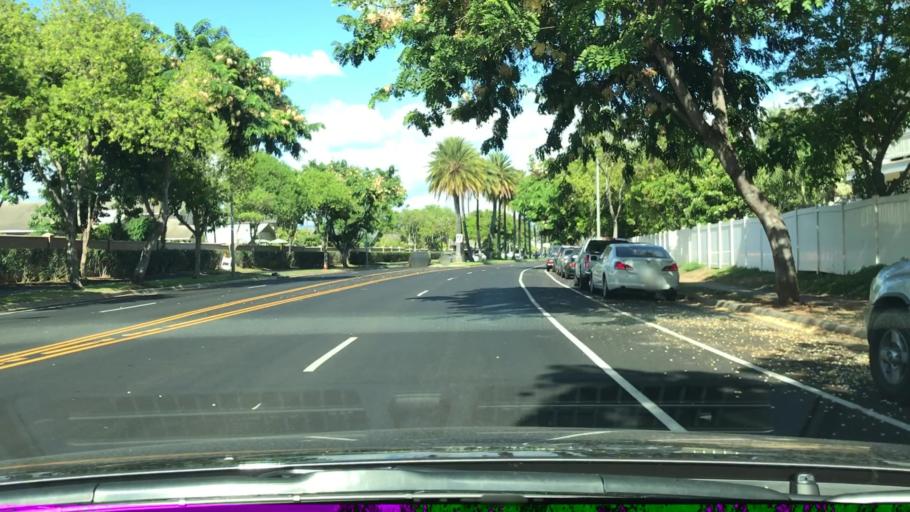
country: US
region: Hawaii
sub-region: Honolulu County
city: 'Ewa Gentry
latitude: 21.3407
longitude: -158.0274
